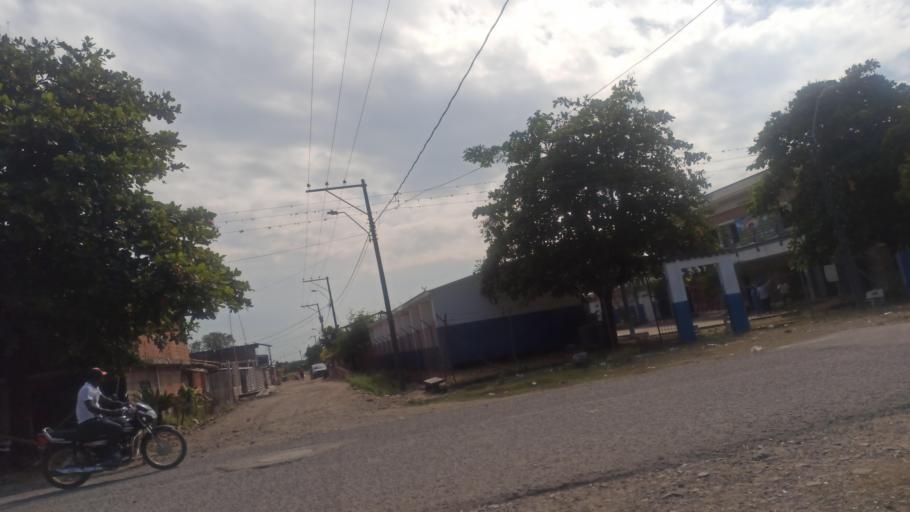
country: CO
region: Valle del Cauca
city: Jamundi
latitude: 3.1289
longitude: -76.5571
